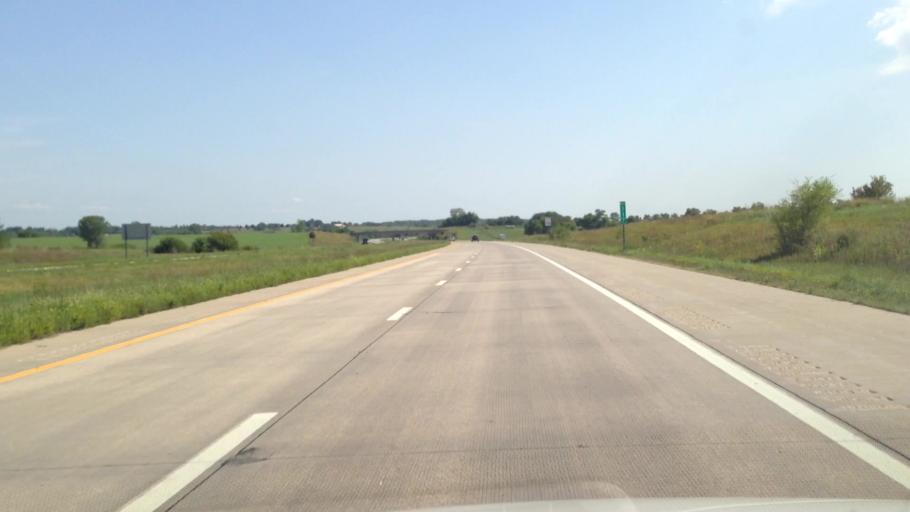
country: US
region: Kansas
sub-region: Miami County
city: Louisburg
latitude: 38.5551
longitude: -94.6910
